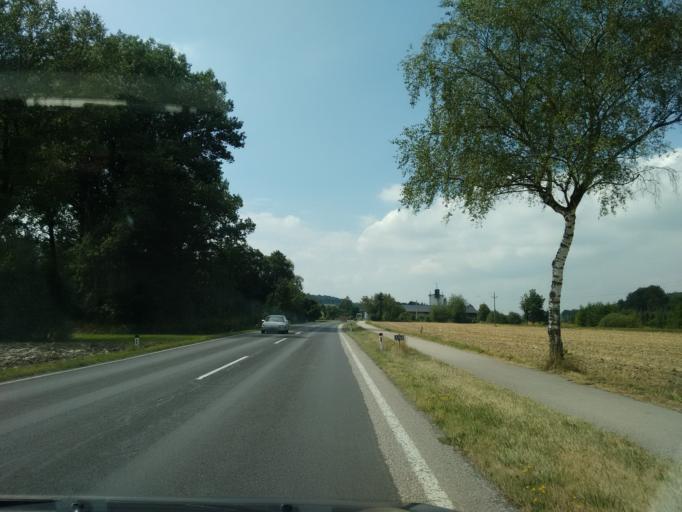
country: AT
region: Upper Austria
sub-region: Politischer Bezirk Grieskirchen
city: Bad Schallerbach
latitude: 48.2188
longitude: 13.8868
